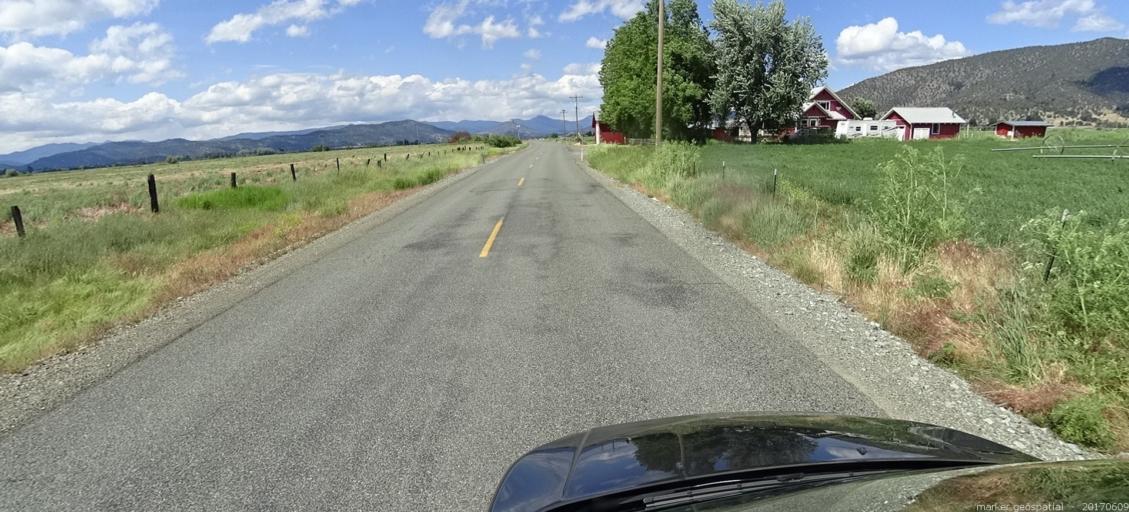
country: US
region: California
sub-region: Siskiyou County
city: Yreka
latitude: 41.4970
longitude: -122.8591
